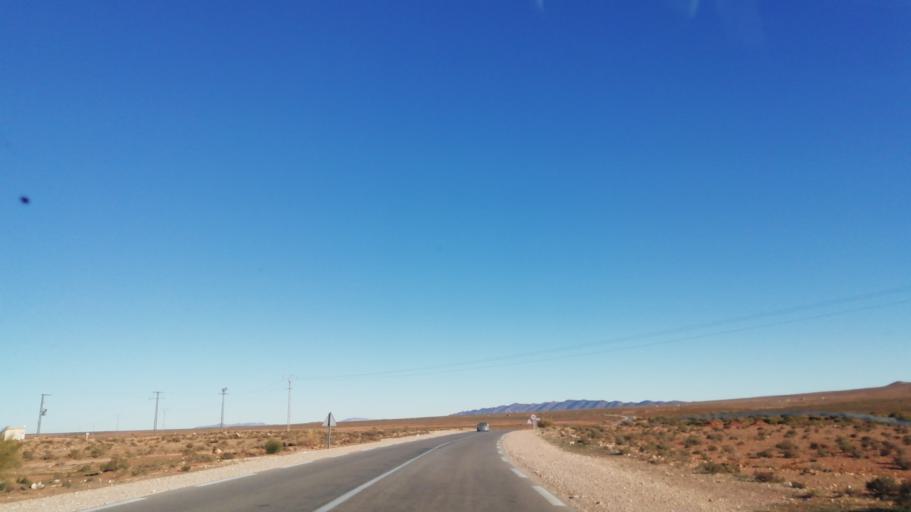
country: DZ
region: El Bayadh
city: El Abiodh Sidi Cheikh
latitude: 33.1149
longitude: 0.2447
